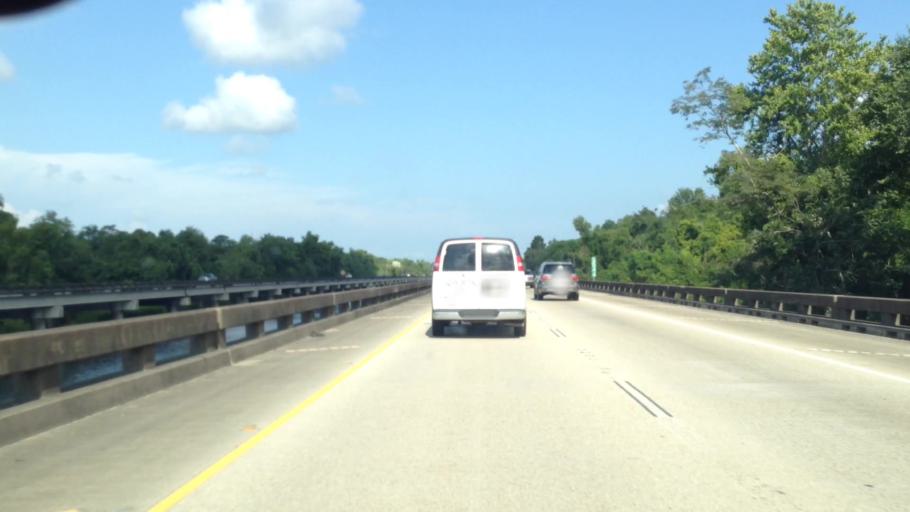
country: US
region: Louisiana
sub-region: Saint John the Baptist Parish
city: Montegut
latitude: 30.1088
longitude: -90.5178
